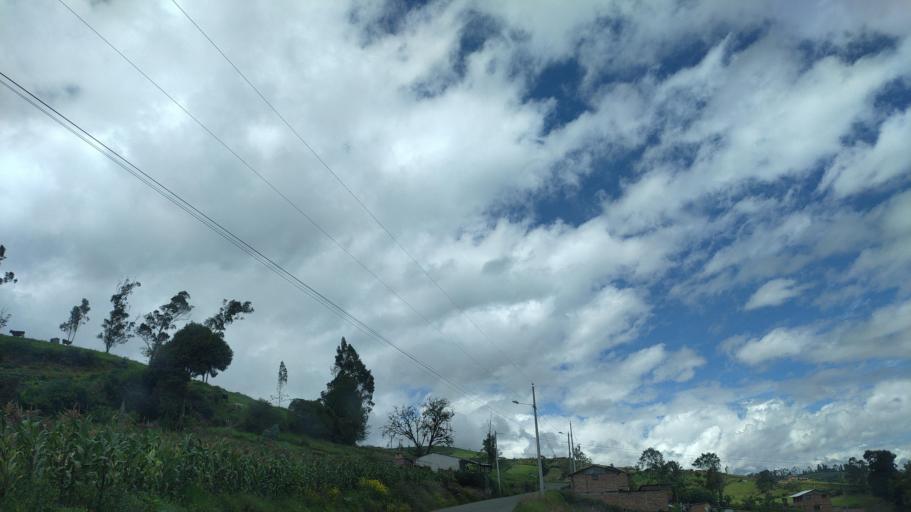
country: EC
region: Chimborazo
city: Riobamba
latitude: -1.6678
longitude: -78.5701
